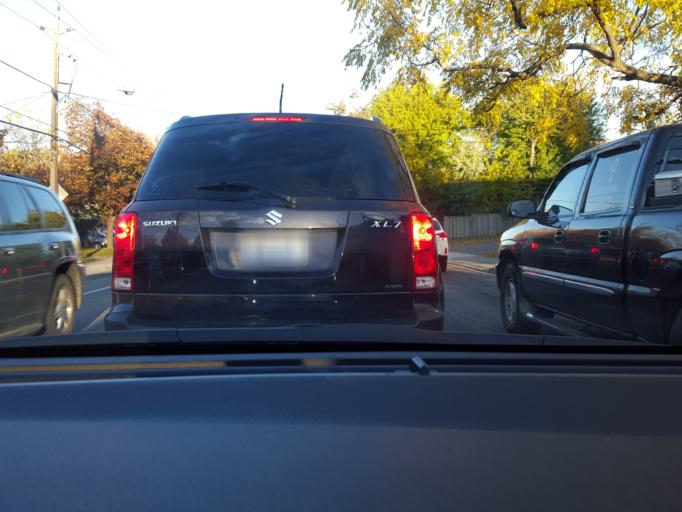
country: CA
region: Ontario
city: Willowdale
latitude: 43.7468
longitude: -79.3901
